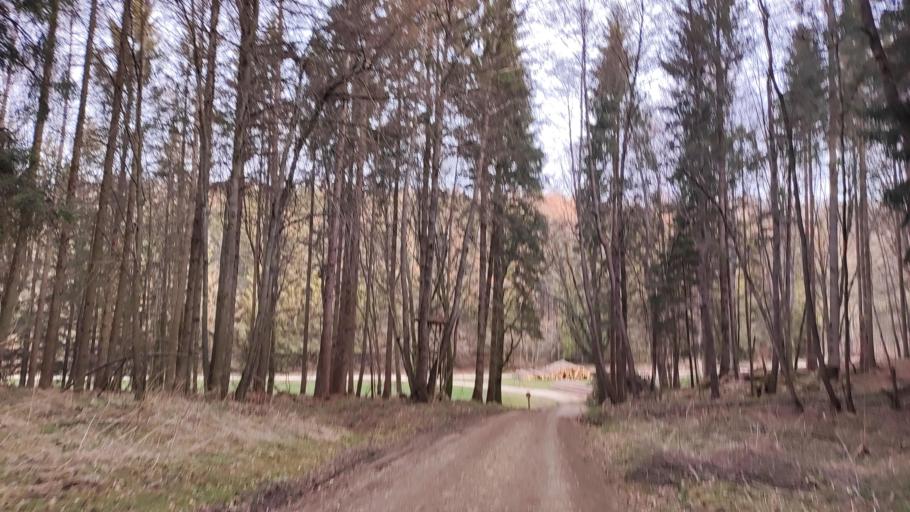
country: DE
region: Bavaria
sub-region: Swabia
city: Zusmarshausen
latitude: 48.4235
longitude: 10.6135
